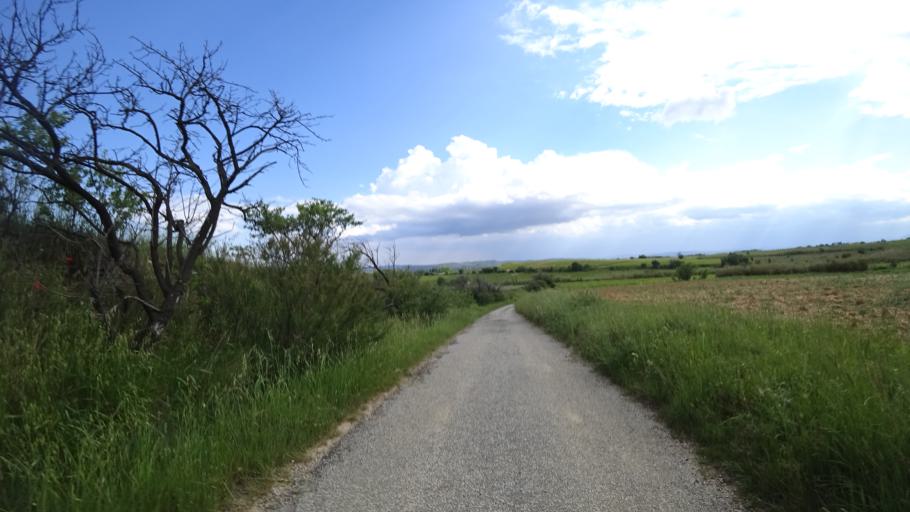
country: FR
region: Languedoc-Roussillon
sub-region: Departement de l'Aude
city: Ginestas
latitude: 43.2582
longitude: 2.8773
